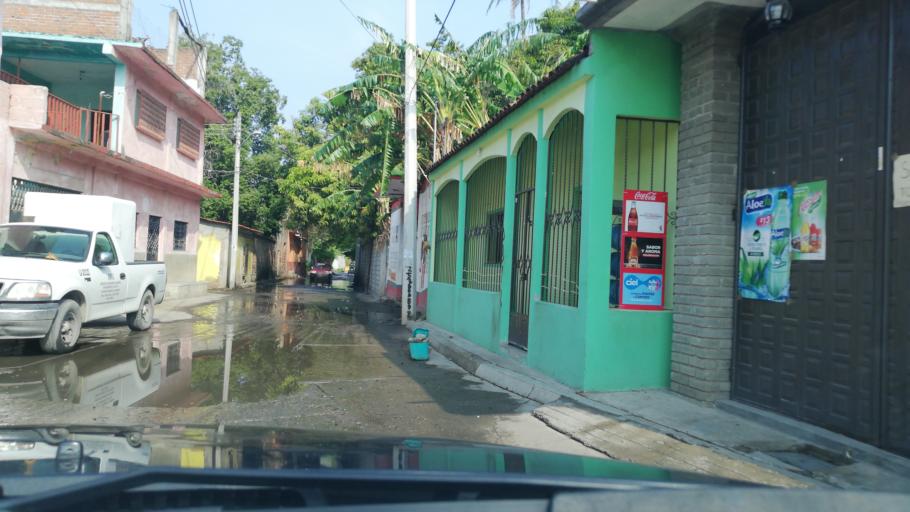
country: MX
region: Oaxaca
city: San Blas Atempa
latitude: 16.3366
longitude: -95.2289
